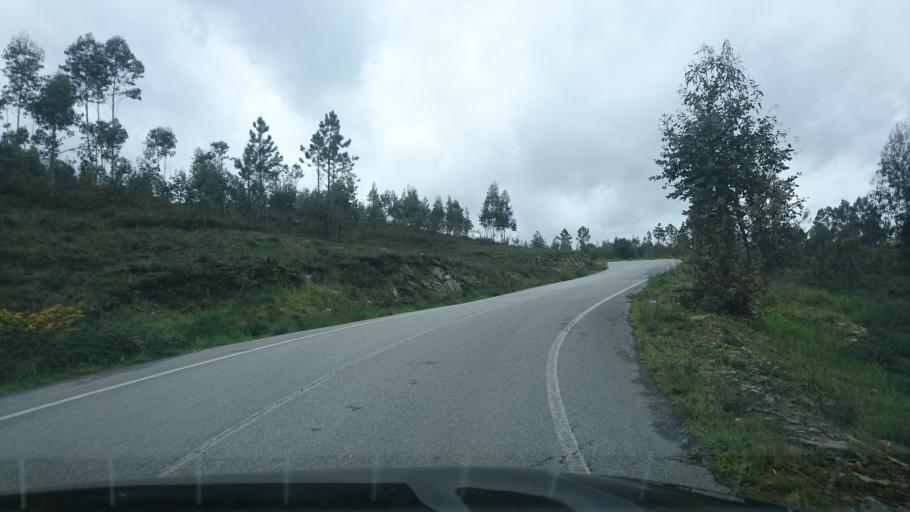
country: PT
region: Porto
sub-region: Paredes
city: Recarei
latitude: 41.1379
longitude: -8.4010
